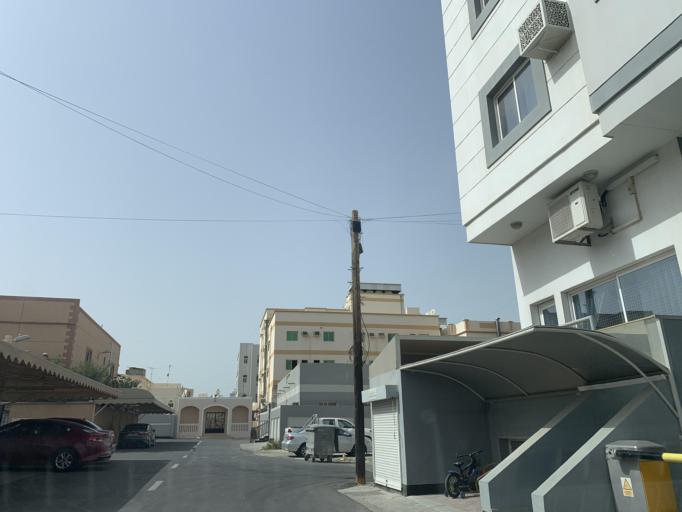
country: BH
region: Northern
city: Ar Rifa'
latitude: 26.1240
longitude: 50.5743
